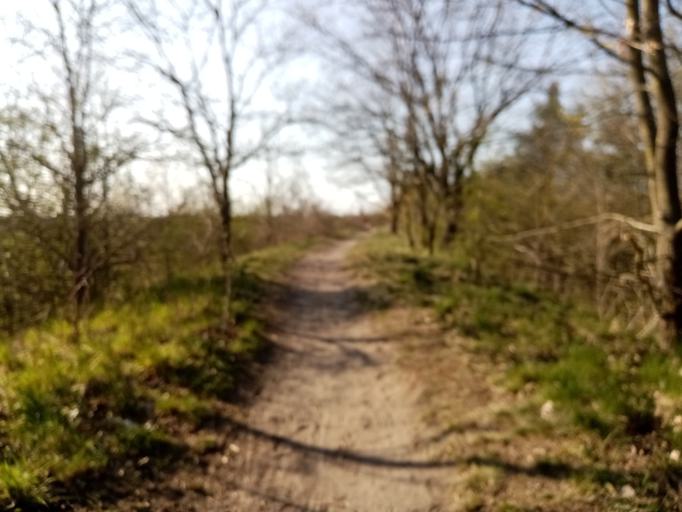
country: DE
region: Berlin
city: Karlshorst
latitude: 52.4705
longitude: 13.5422
